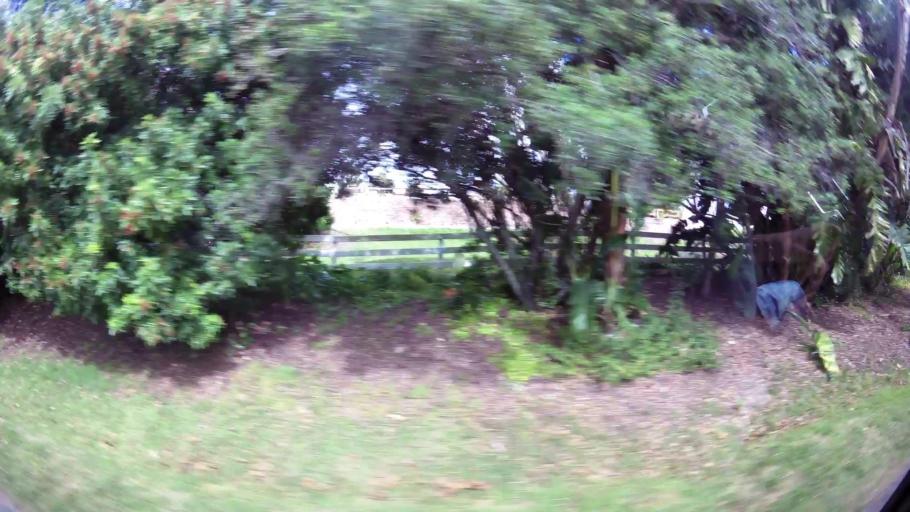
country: ZA
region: Western Cape
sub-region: Eden District Municipality
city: Knysna
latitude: -34.0617
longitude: 23.0820
